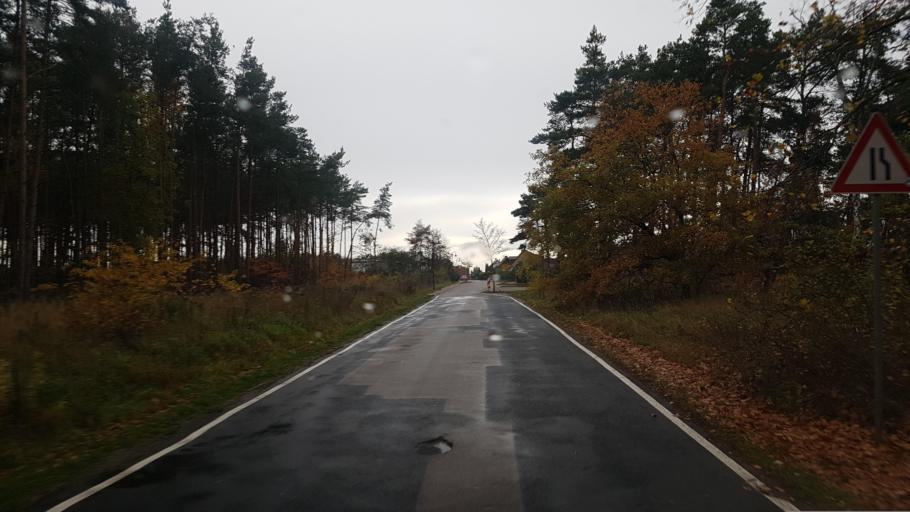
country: DE
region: Saxony-Anhalt
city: Abtsdorf
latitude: 51.8855
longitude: 12.7286
